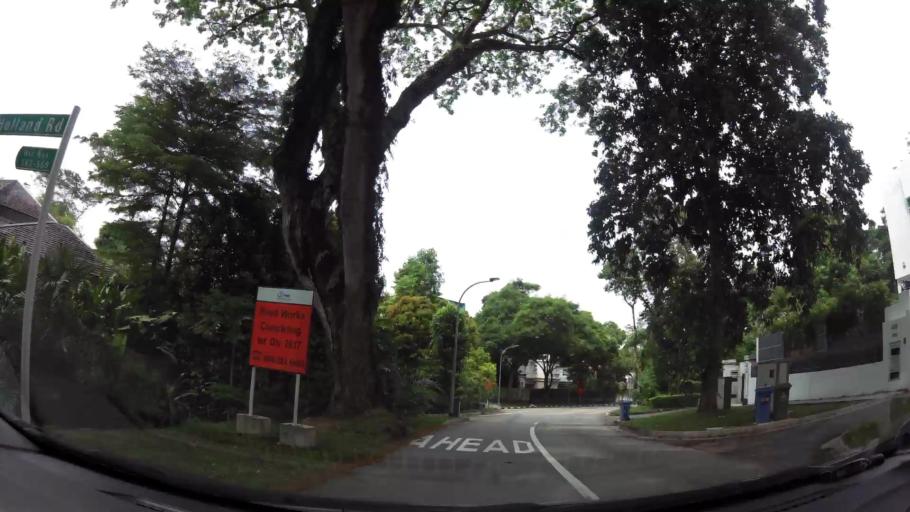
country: SG
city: Singapore
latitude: 1.3248
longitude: 103.7849
